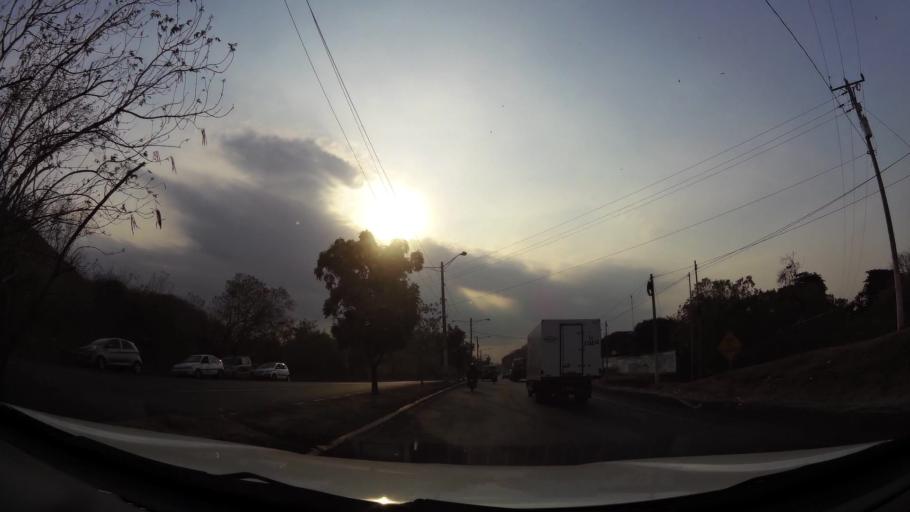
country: NI
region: Managua
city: Ciudad Sandino
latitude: 12.1327
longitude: -86.3210
